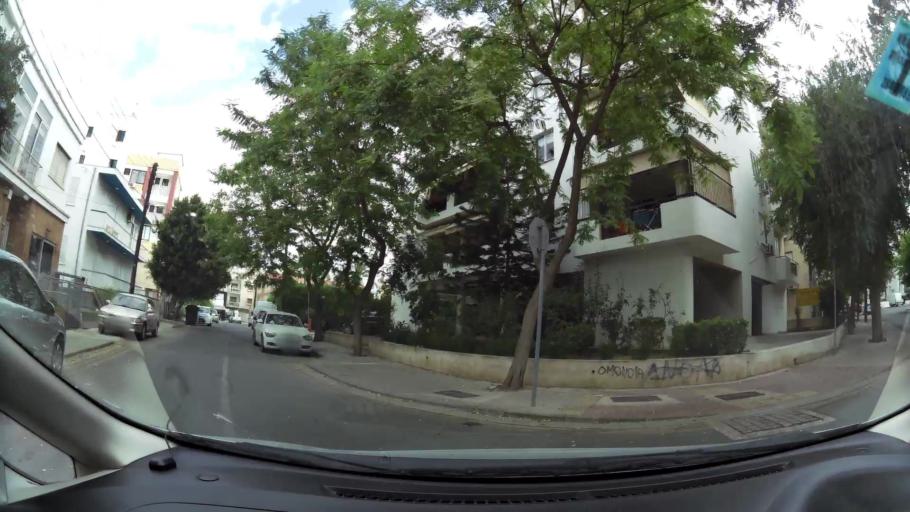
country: CY
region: Lefkosia
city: Nicosia
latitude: 35.1646
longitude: 33.3713
